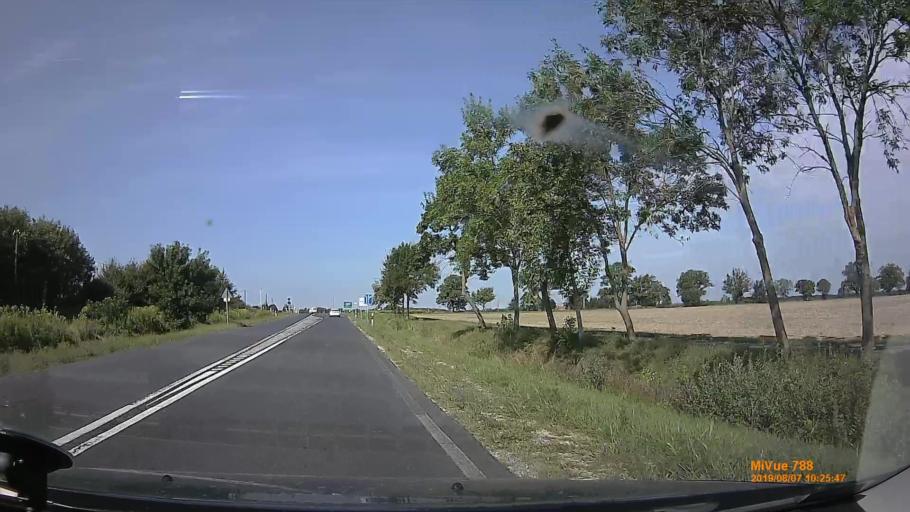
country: HU
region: Zala
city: Lenti
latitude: 46.6202
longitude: 16.4891
